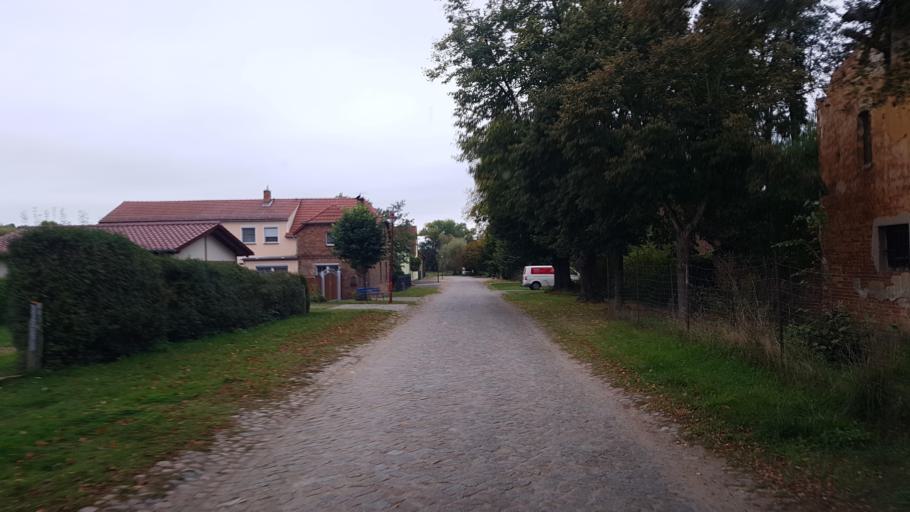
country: DE
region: Brandenburg
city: Drahnsdorf
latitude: 51.8913
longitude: 13.6423
